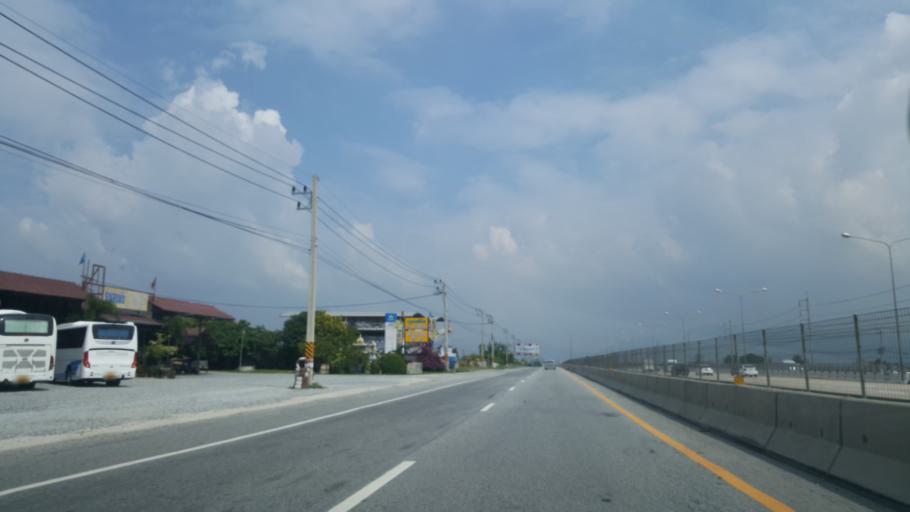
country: TH
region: Chon Buri
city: Si Racha
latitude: 13.1669
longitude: 100.9906
